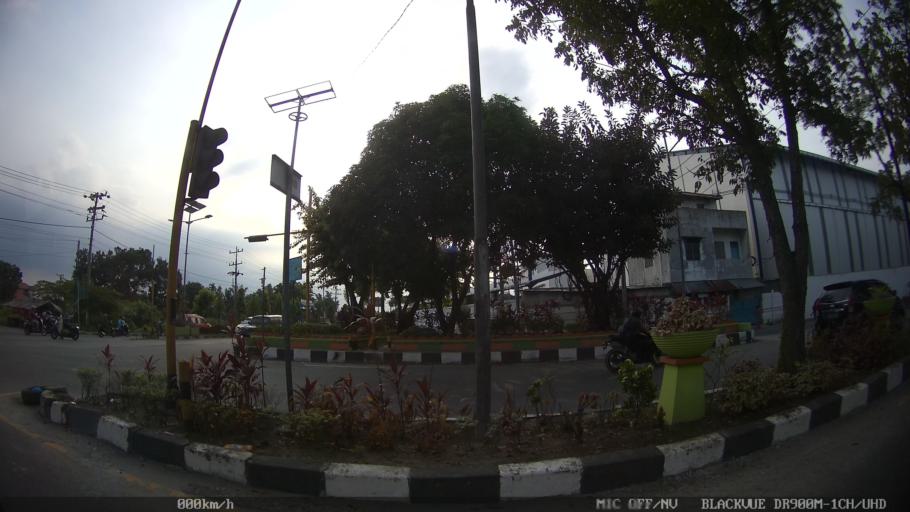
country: ID
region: North Sumatra
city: Binjai
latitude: 3.6049
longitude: 98.5339
